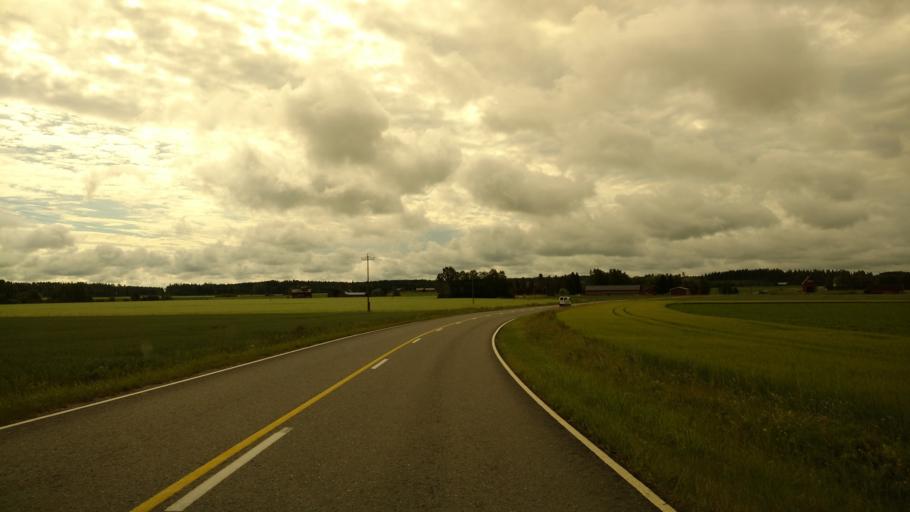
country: FI
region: Varsinais-Suomi
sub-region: Salo
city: Kuusjoki
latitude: 60.5191
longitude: 23.1773
